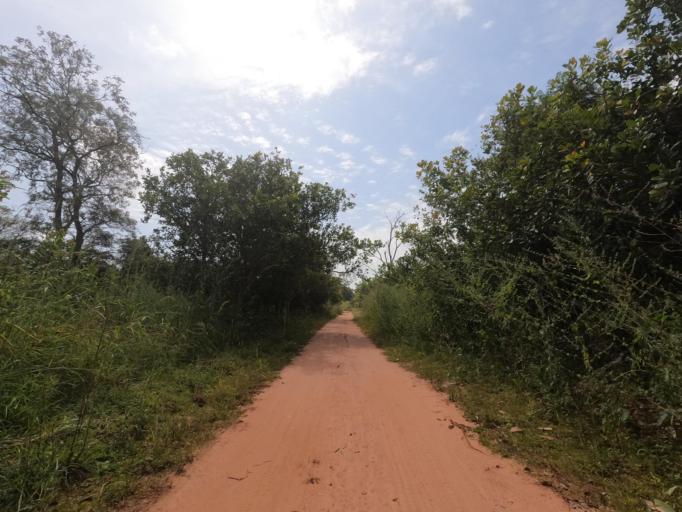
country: GW
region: Oio
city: Bissora
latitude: 12.3851
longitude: -15.7157
